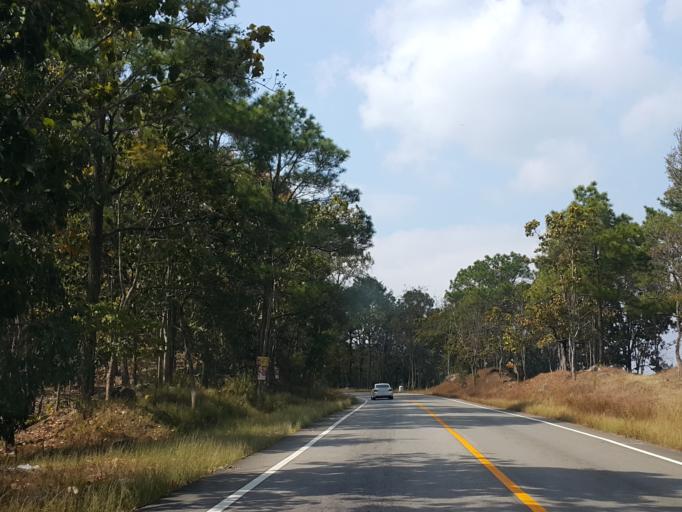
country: TH
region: Chiang Mai
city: Hot
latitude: 18.1579
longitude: 98.4082
